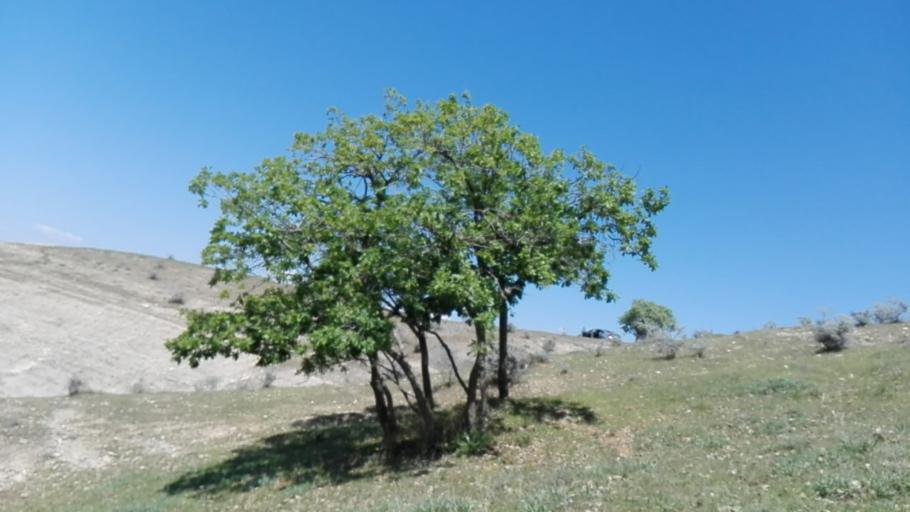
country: TR
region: Diyarbakir
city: Malabadi
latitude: 38.1771
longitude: 41.2181
